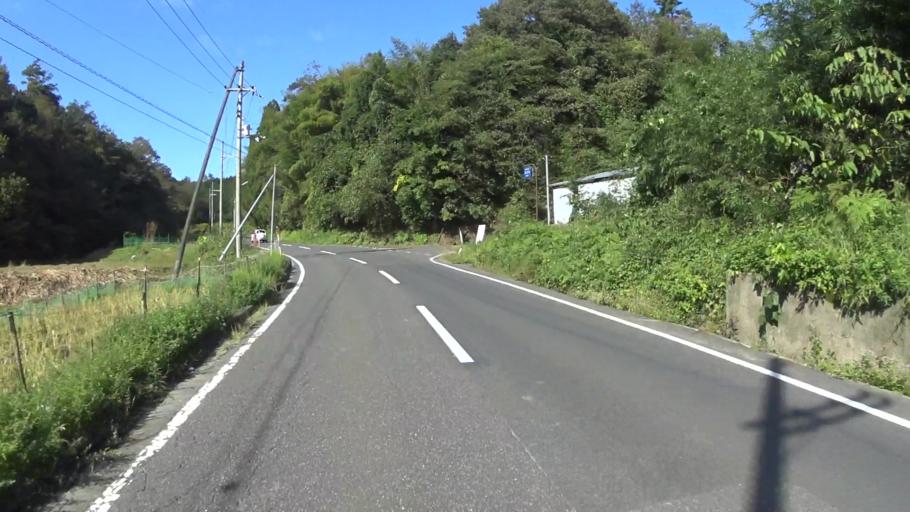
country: JP
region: Kyoto
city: Miyazu
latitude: 35.5933
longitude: 135.1539
